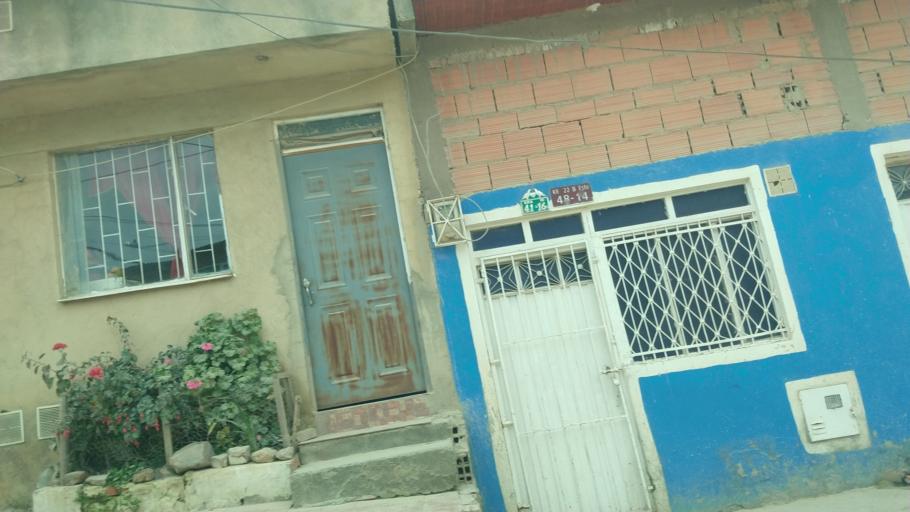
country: CO
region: Cundinamarca
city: Soacha
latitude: 4.5820
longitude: -74.1853
